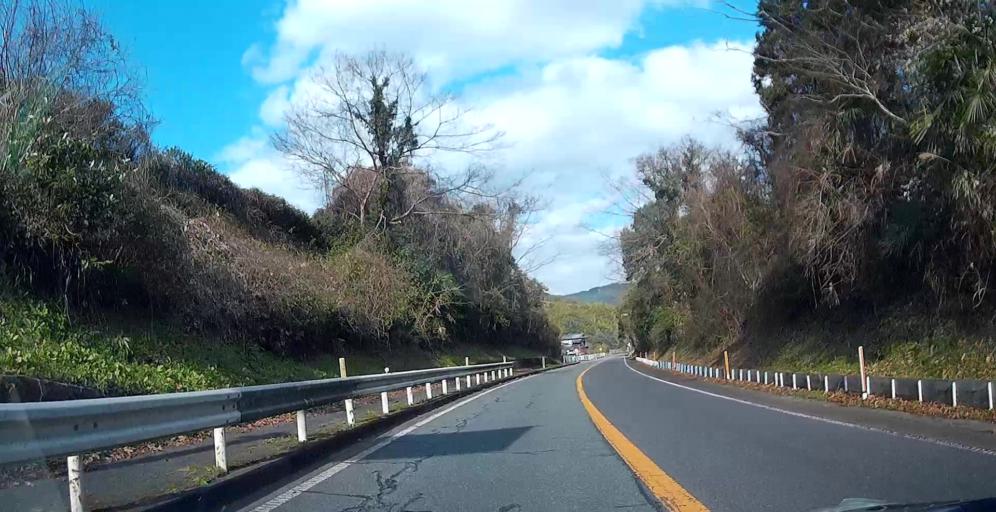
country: JP
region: Kumamoto
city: Yatsushiro
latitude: 32.3924
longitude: 130.5445
